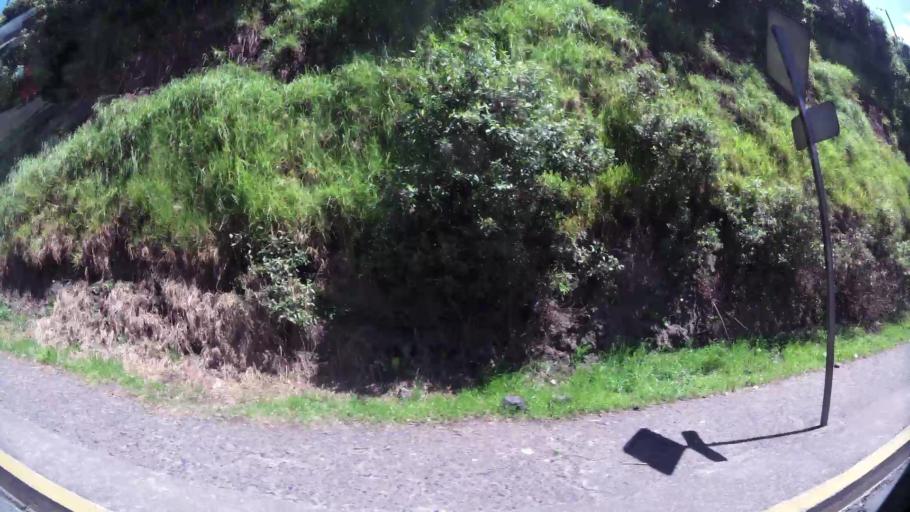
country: EC
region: Pichincha
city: Quito
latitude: -0.3207
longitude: -78.5644
